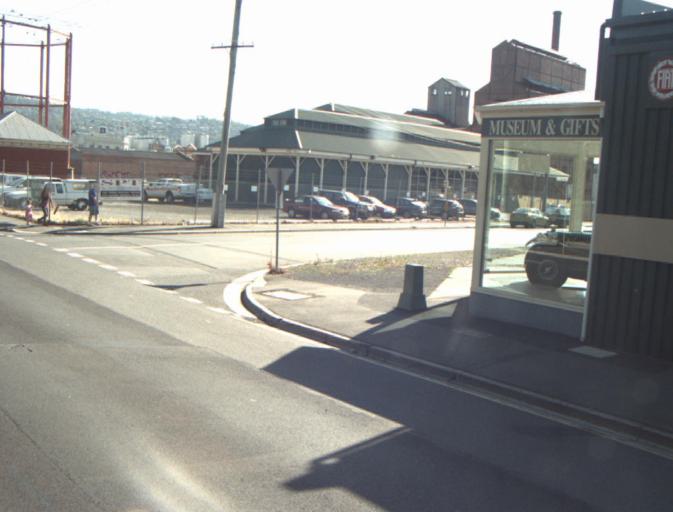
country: AU
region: Tasmania
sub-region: Launceston
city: East Launceston
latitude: -41.4318
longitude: 147.1429
